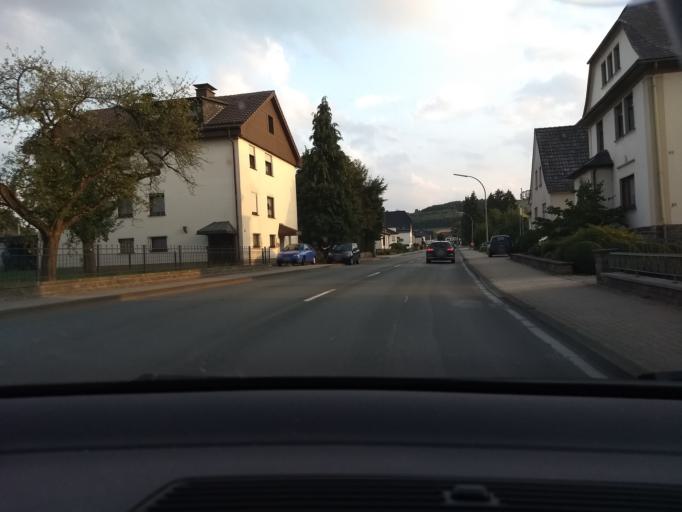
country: DE
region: North Rhine-Westphalia
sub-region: Regierungsbezirk Arnsberg
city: Arnsberg
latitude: 51.3601
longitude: 8.1705
